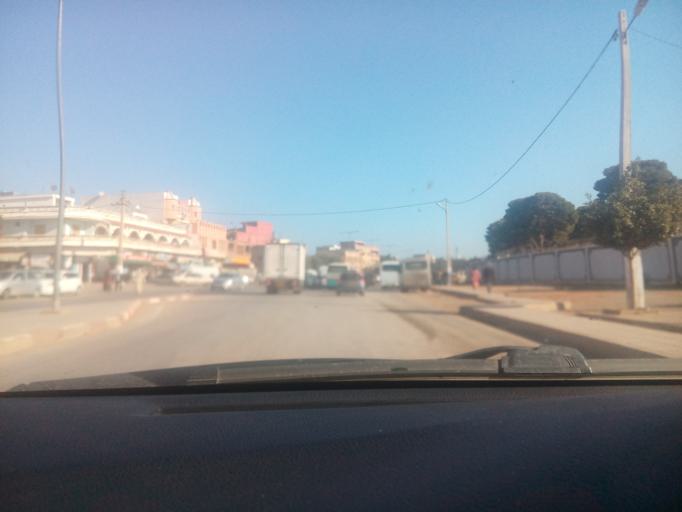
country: DZ
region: Oran
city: Oran
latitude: 35.6594
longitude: -0.6957
